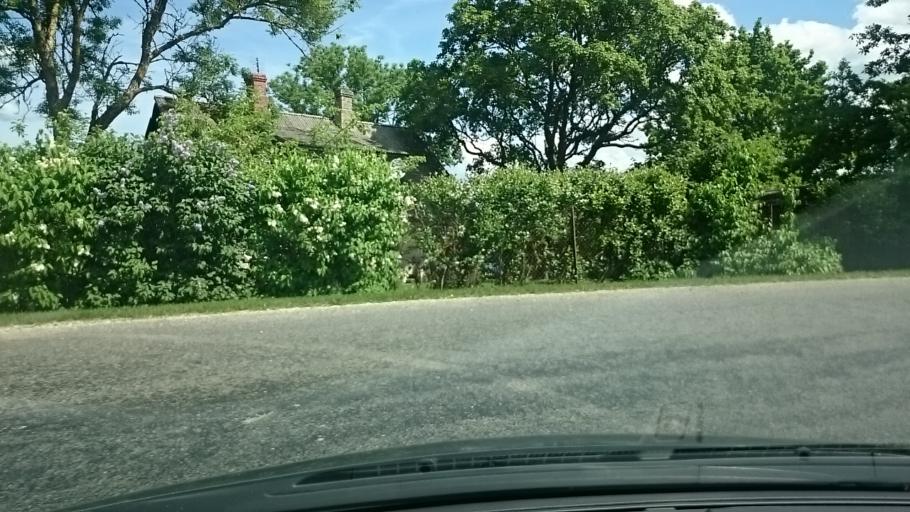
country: EE
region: Harju
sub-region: Anija vald
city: Kehra
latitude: 59.0981
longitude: 25.2856
